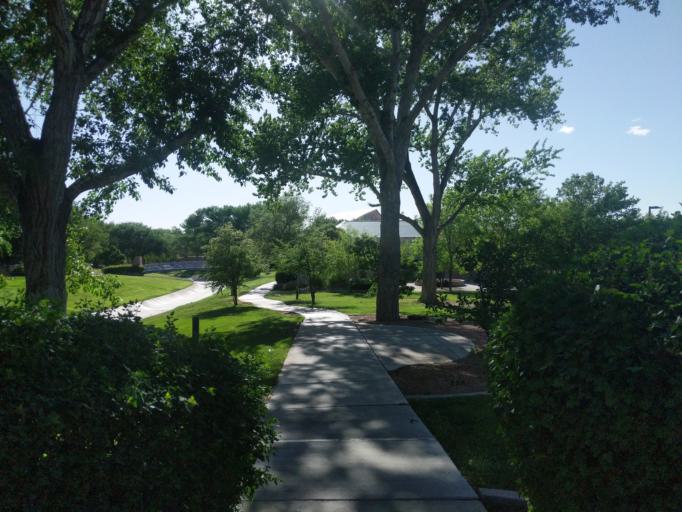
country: US
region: New Mexico
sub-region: Bernalillo County
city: North Valley
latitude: 35.1656
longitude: -106.5871
